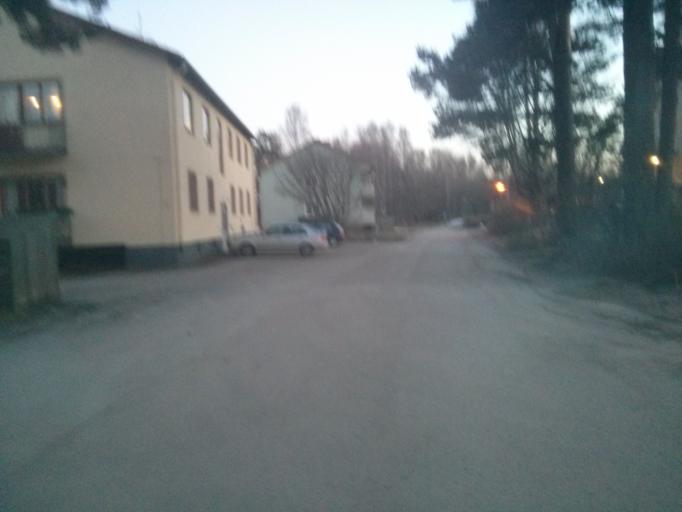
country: SE
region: Vaesternorrland
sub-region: Sundsvalls Kommun
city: Kvissleby
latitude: 62.2949
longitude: 17.3813
